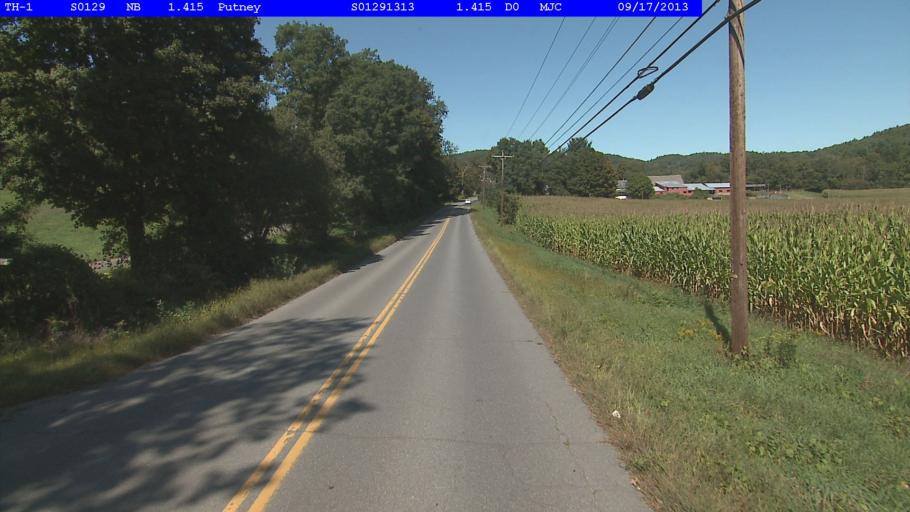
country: US
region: New Hampshire
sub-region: Cheshire County
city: Westmoreland
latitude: 42.9930
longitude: -72.5317
